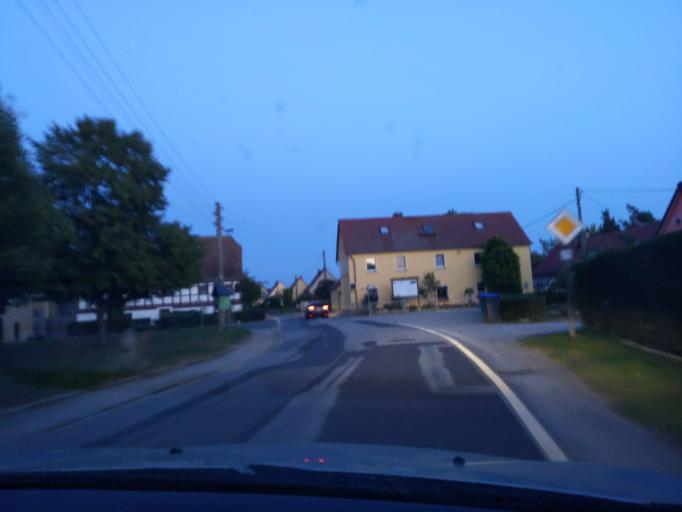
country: DE
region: Saxony
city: Grossdubrau
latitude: 51.2975
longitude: 14.4575
